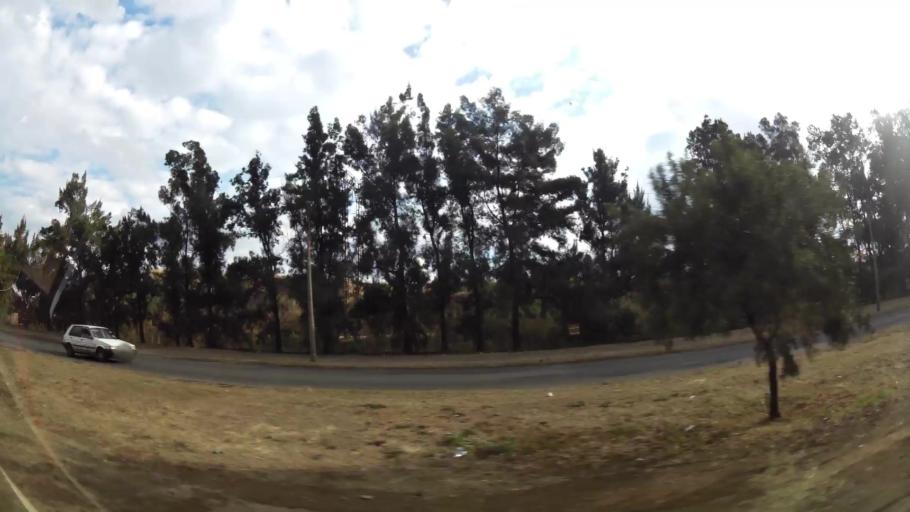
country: ZA
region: Orange Free State
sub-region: Fezile Dabi District Municipality
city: Sasolburg
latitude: -26.8287
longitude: 27.8393
